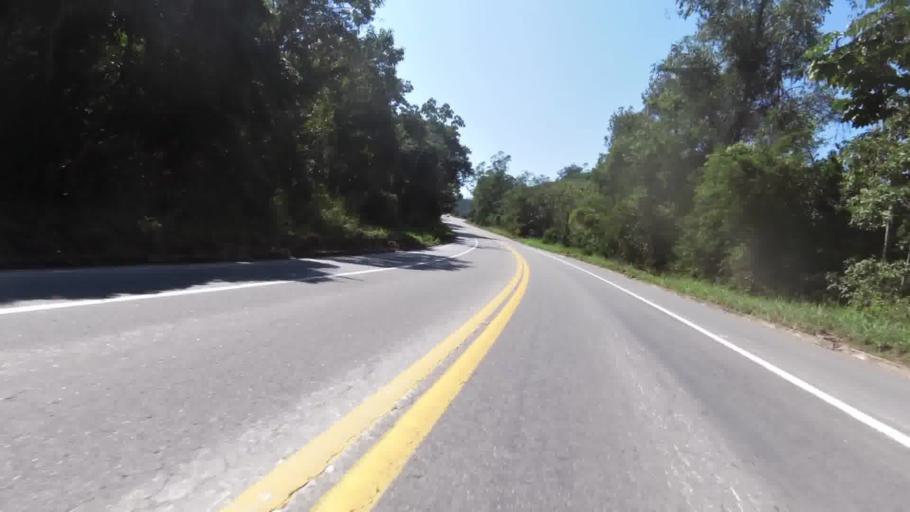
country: BR
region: Espirito Santo
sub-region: Marechal Floriano
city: Marechal Floriano
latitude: -20.4153
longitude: -40.8459
